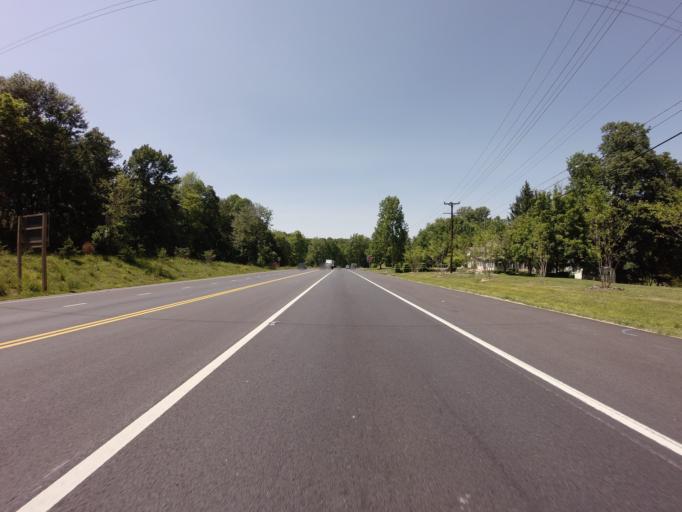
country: US
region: Maryland
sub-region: Carroll County
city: Sykesville
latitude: 39.3569
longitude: -76.9683
